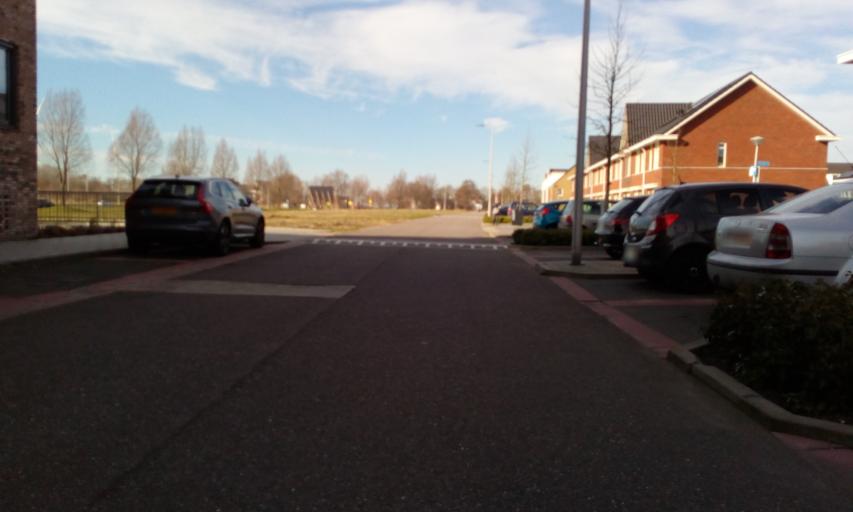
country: NL
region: South Holland
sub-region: Gemeente Alphen aan den Rijn
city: Alphen aan den Rijn
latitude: 52.1191
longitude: 4.6368
